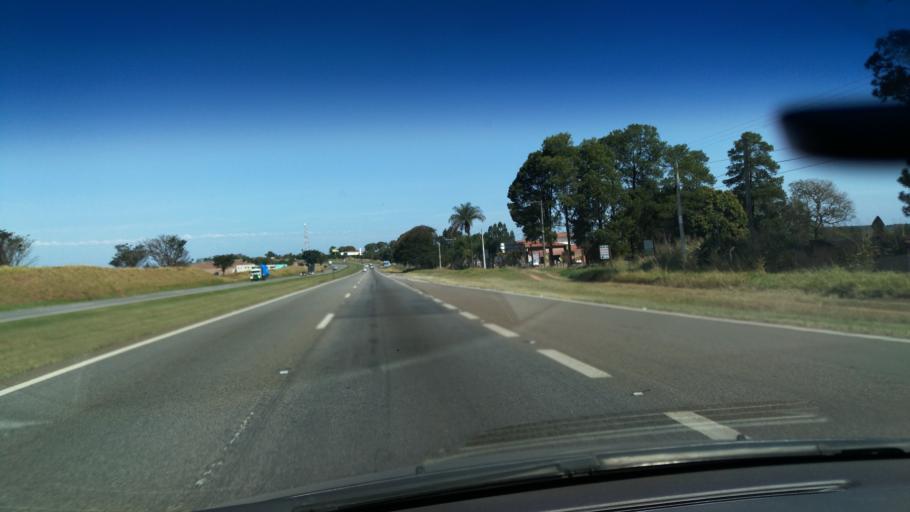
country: BR
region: Sao Paulo
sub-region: Mogi-Mirim
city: Mogi Mirim
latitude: -22.5076
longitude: -46.9877
